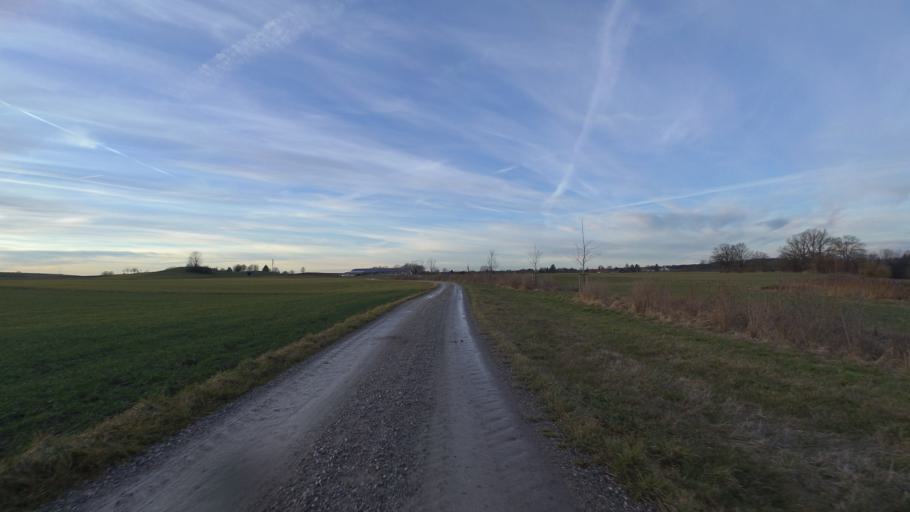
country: DE
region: Bavaria
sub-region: Upper Bavaria
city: Chieming
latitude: 47.8836
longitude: 12.5506
